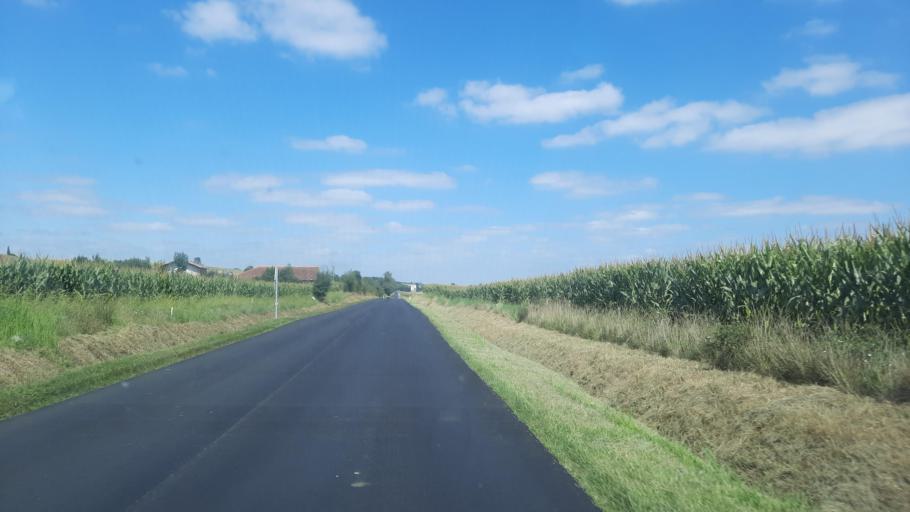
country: FR
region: Midi-Pyrenees
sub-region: Departement du Gers
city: Lombez
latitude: 43.4502
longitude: 0.8724
